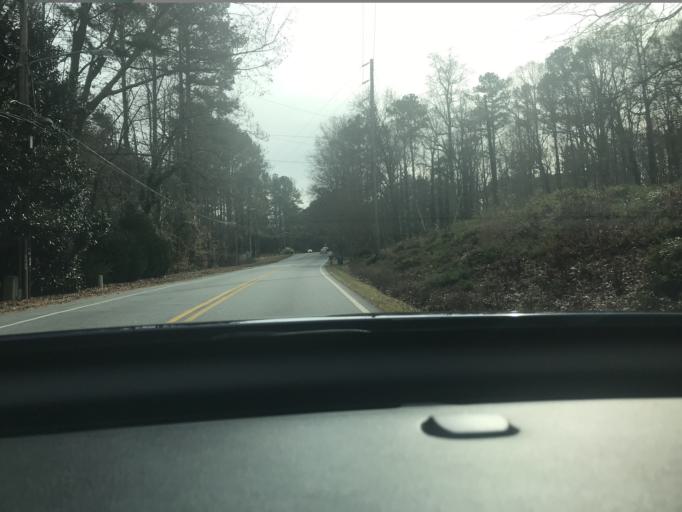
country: US
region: Georgia
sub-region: Gwinnett County
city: Lilburn
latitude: 33.8914
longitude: -84.0941
